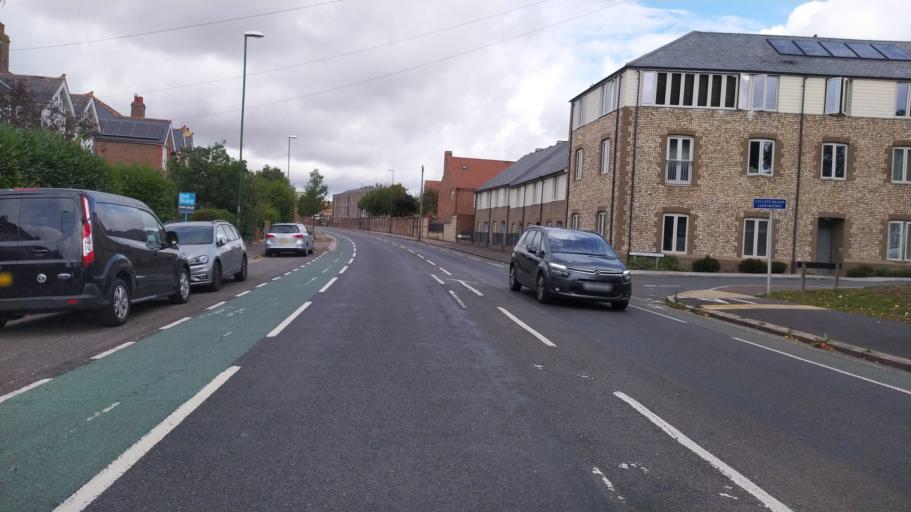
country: GB
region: England
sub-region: West Sussex
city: Chichester
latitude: 50.8486
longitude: -0.7795
